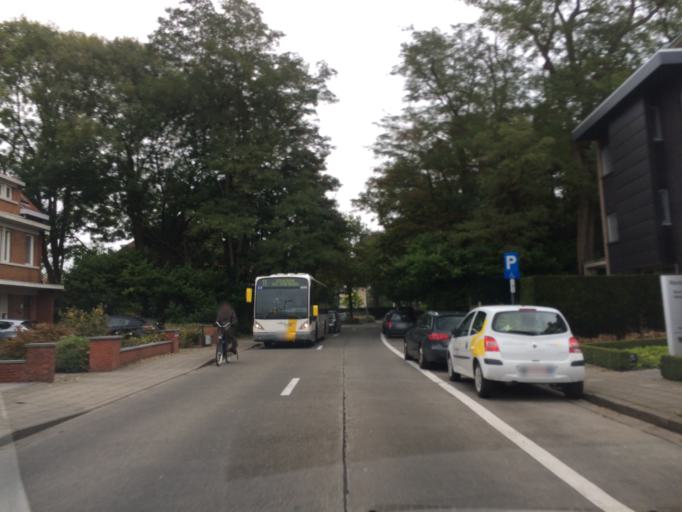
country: BE
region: Flanders
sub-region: Provincie West-Vlaanderen
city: Sint-Kruis
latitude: 51.2011
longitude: 3.2485
